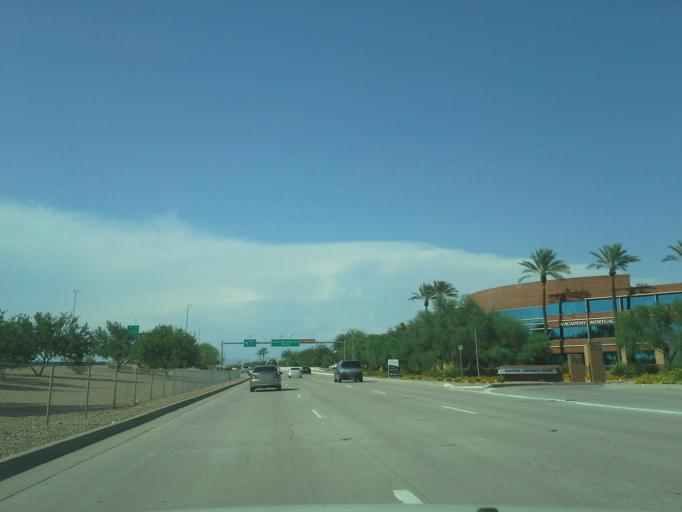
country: US
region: Arizona
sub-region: Maricopa County
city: Paradise Valley
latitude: 33.6239
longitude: -111.8901
